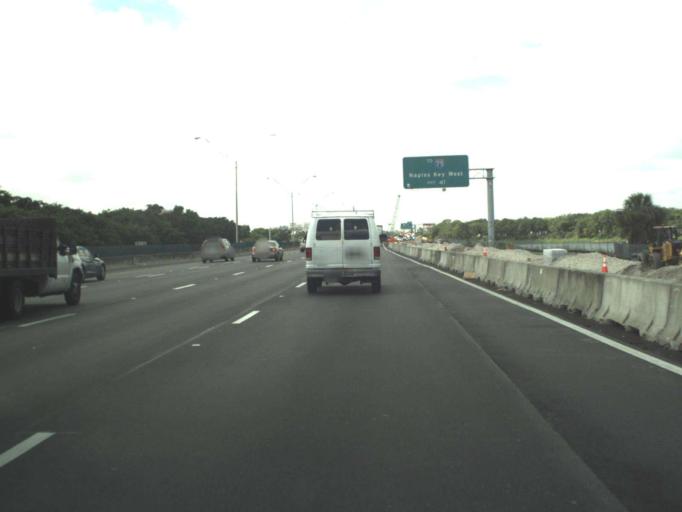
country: US
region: Florida
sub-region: Broward County
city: Deerfield Beach
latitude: 26.3123
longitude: -80.1175
